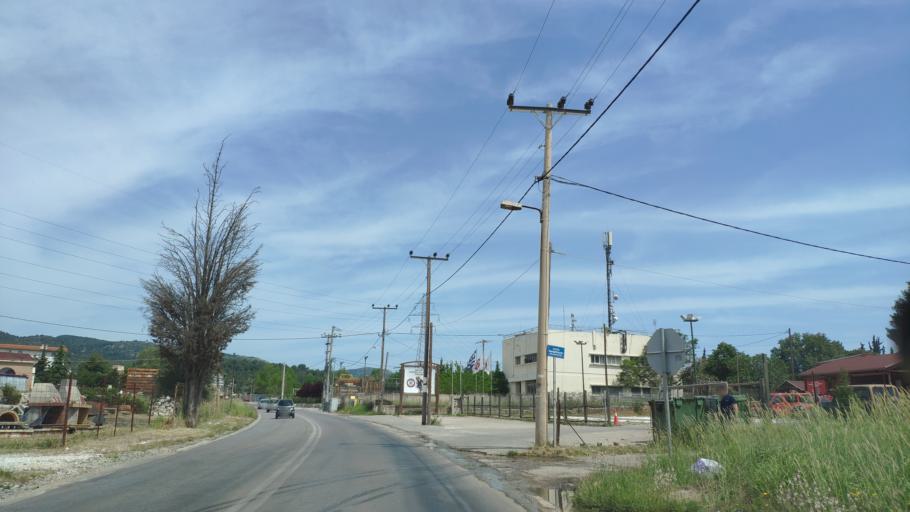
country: GR
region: Attica
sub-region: Nomarchia Anatolikis Attikis
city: Afidnes
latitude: 38.1928
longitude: 23.8539
